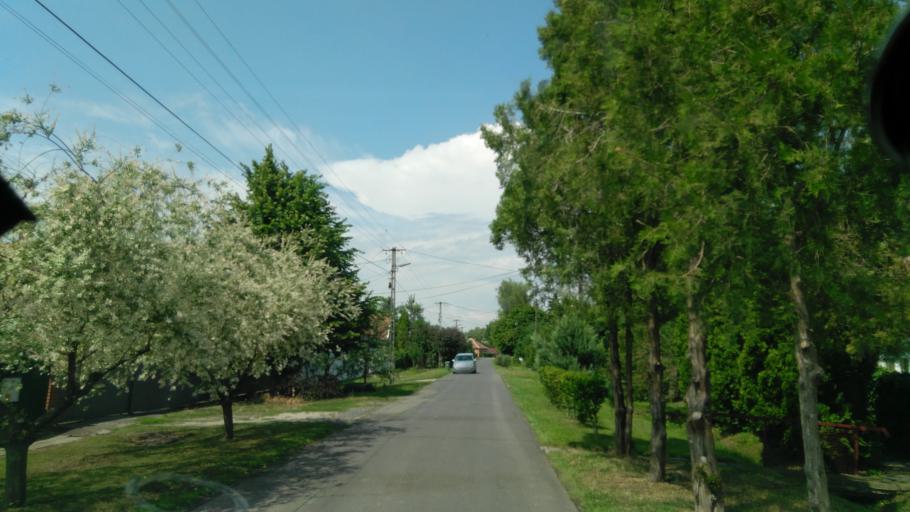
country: HU
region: Bekes
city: Bekes
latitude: 46.7624
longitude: 21.1478
